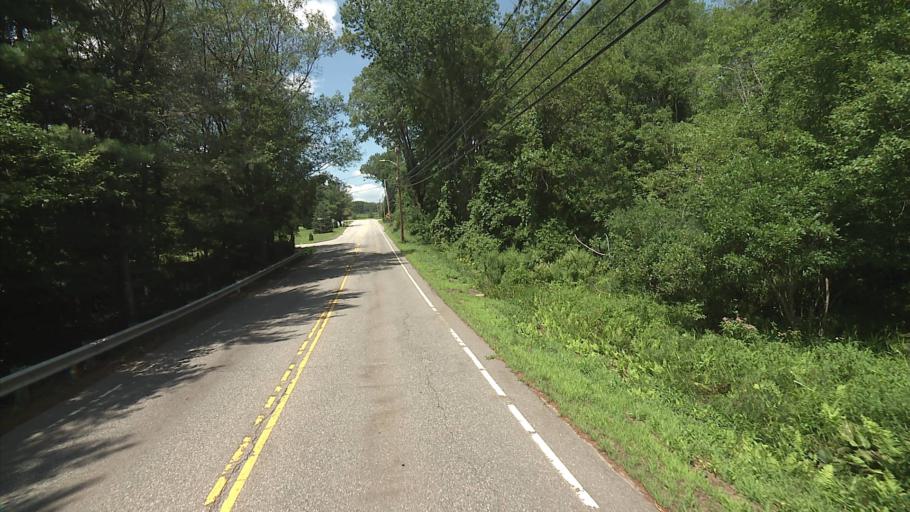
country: US
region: Connecticut
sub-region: Windham County
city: Windham
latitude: 41.7001
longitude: -72.1415
